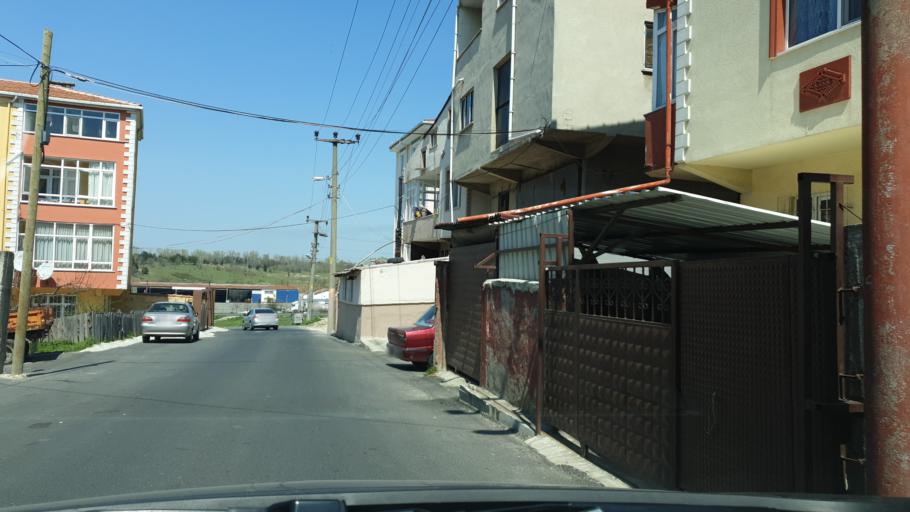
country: TR
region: Tekirdag
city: Corlu
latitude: 41.1664
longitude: 27.7903
